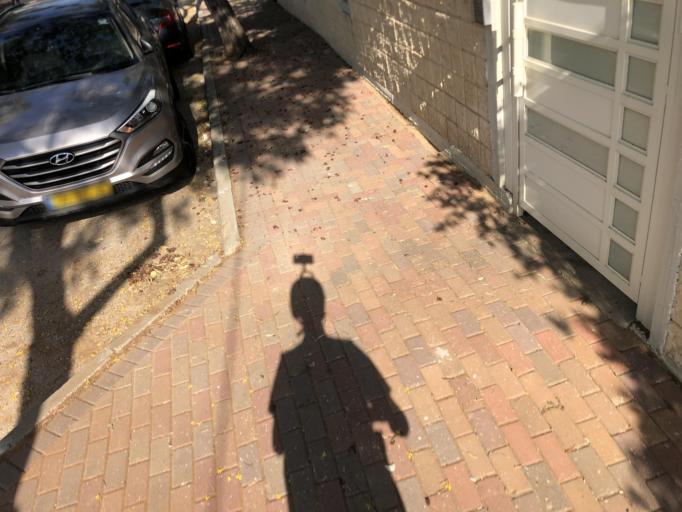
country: IL
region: Central District
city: Yehud
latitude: 32.0369
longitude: 34.8959
